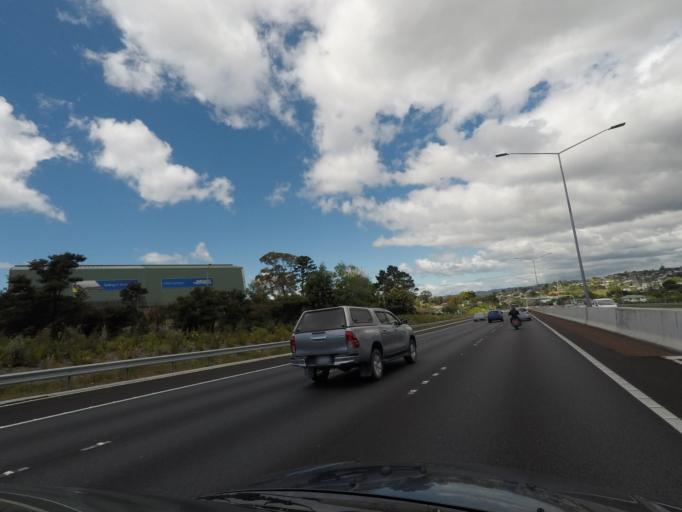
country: NZ
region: Auckland
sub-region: Auckland
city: Rosebank
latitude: -36.8325
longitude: 174.6195
